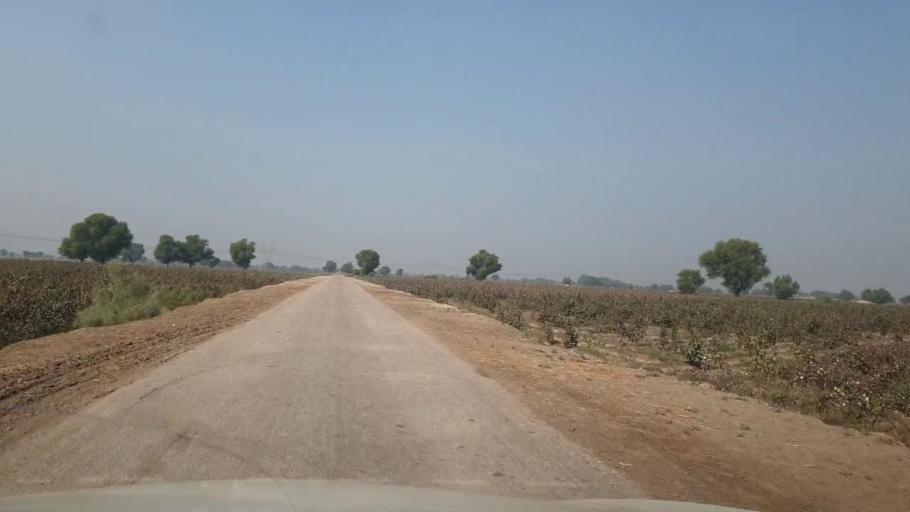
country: PK
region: Sindh
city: Bhan
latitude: 26.5298
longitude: 67.7546
